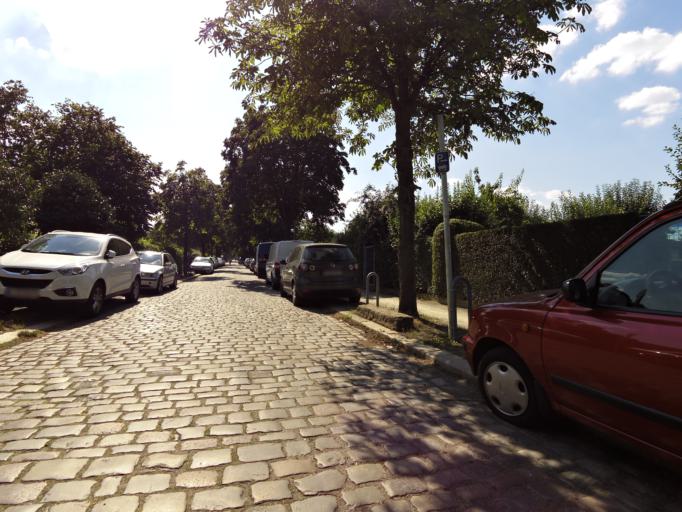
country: DE
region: Berlin
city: Schoneberg Bezirk
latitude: 52.4619
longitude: 13.3556
